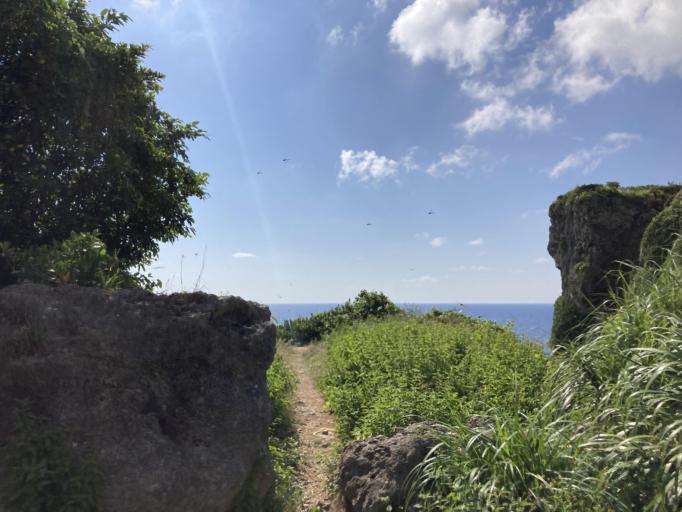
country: JP
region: Okinawa
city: Itoman
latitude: 26.1012
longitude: 127.7344
